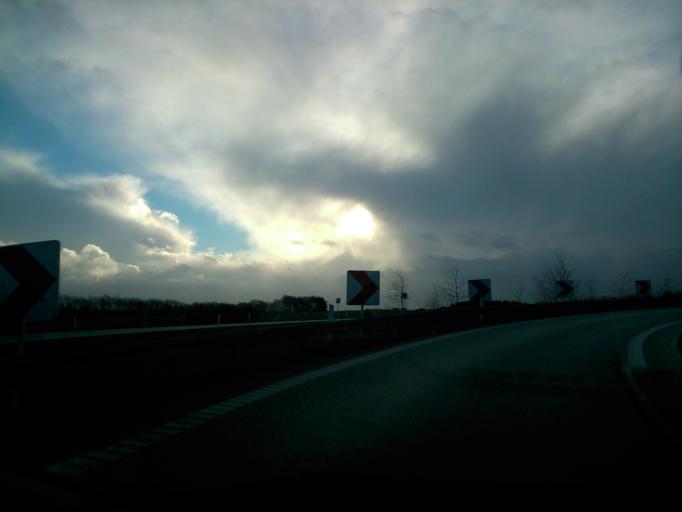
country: DK
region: Central Jutland
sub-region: Herning Kommune
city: Lind
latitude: 56.1098
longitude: 9.0118
